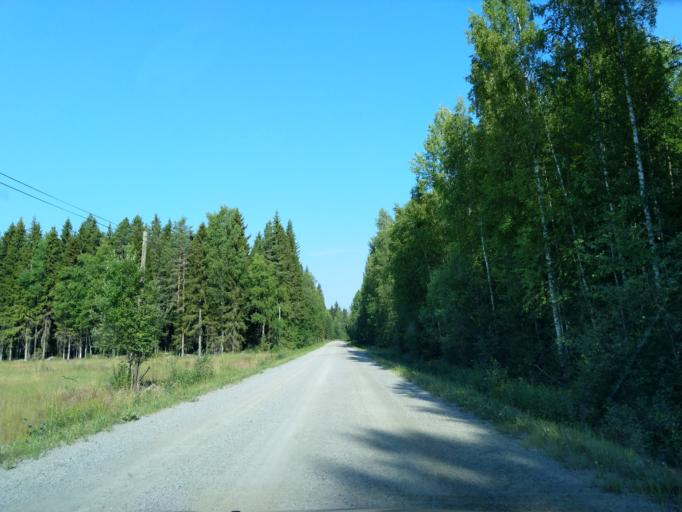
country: FI
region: Satakunta
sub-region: Pori
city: Laengelmaeki
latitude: 61.7313
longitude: 22.1774
